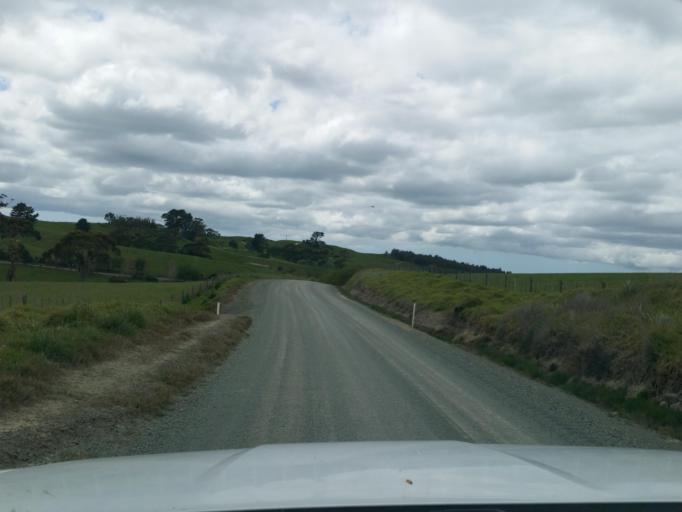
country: NZ
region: Auckland
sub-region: Auckland
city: Wellsford
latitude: -36.2761
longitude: 174.3679
